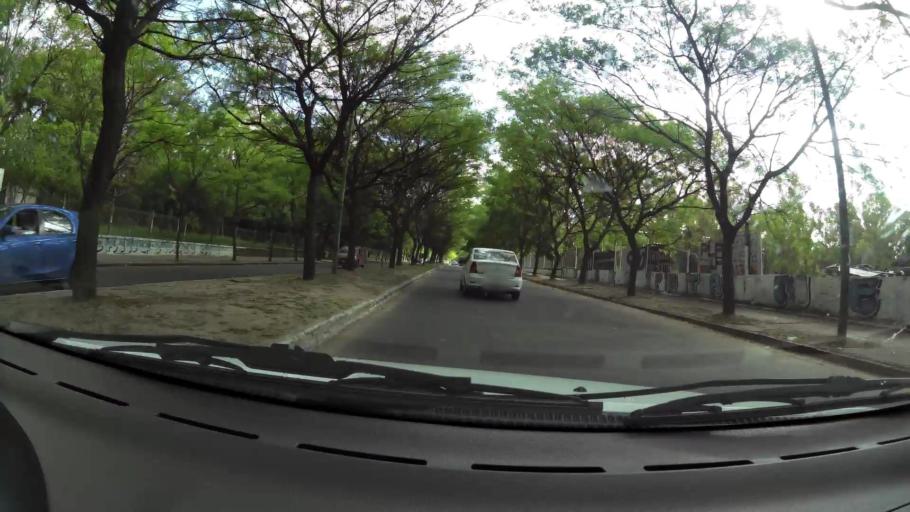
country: AR
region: Buenos Aires
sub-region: Partido de La Plata
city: La Plata
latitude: -34.9120
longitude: -57.9318
